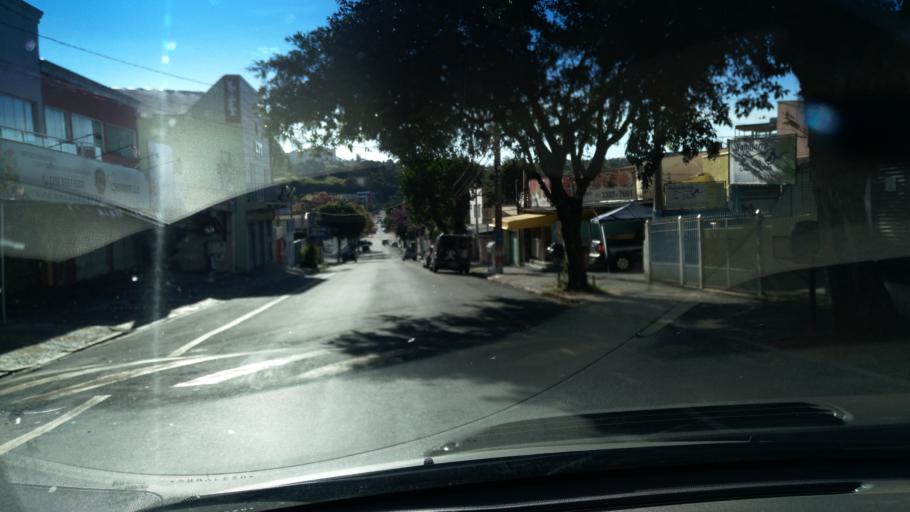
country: BR
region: Sao Paulo
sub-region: Valinhos
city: Valinhos
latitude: -22.9654
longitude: -47.0014
